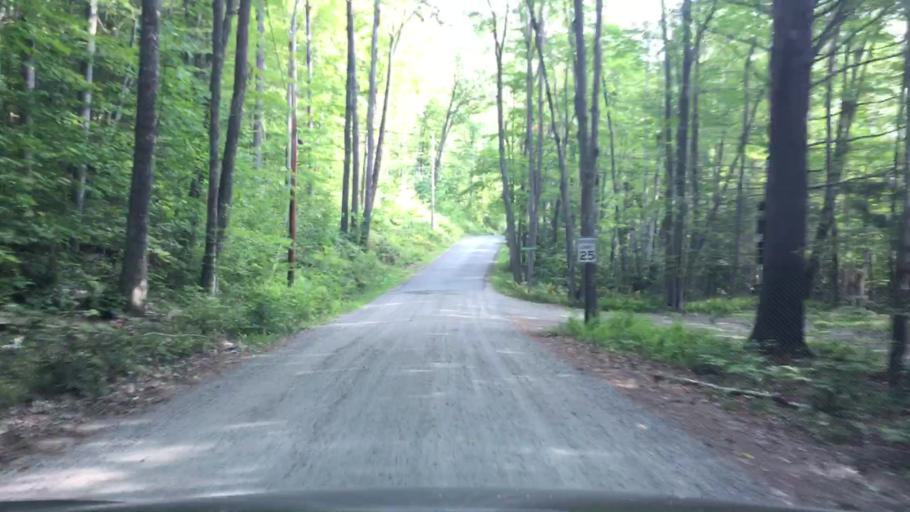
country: US
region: New Hampshire
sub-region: Grafton County
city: Littleton
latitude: 44.3081
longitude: -71.8911
